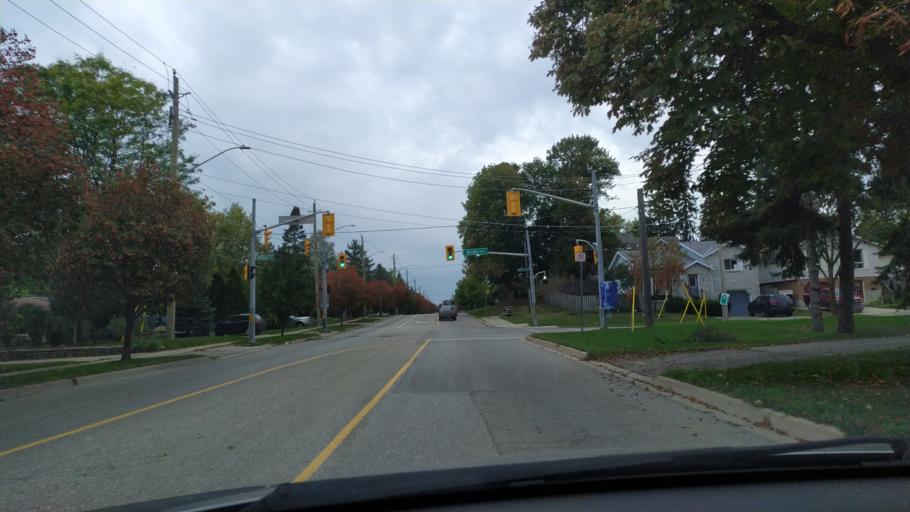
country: CA
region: Ontario
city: Waterloo
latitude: 43.4849
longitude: -80.4878
